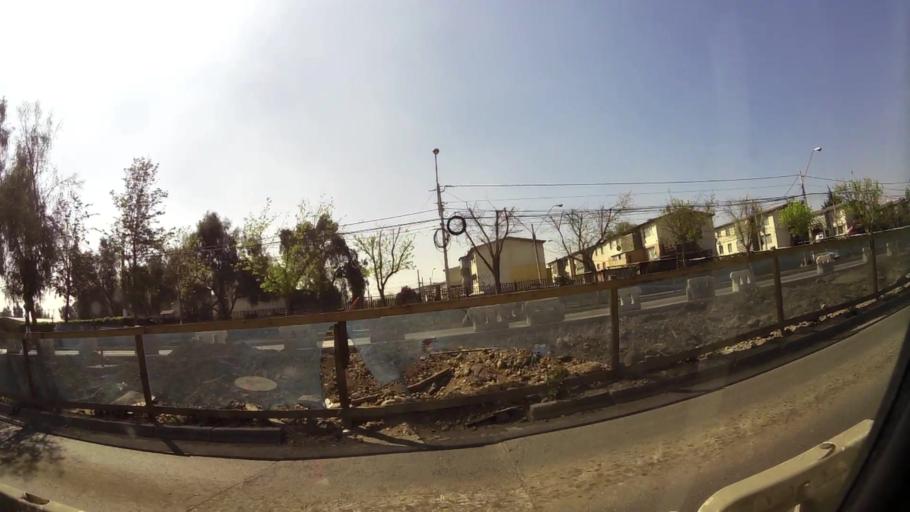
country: CL
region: Santiago Metropolitan
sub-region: Provincia de Santiago
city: Lo Prado
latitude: -33.5063
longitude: -70.7861
